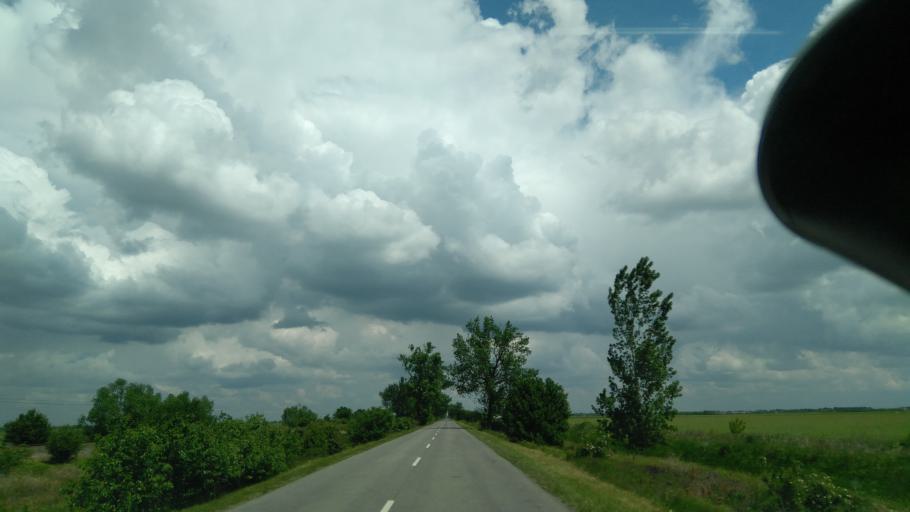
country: HU
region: Bekes
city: Devavanya
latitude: 47.0000
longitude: 20.9115
